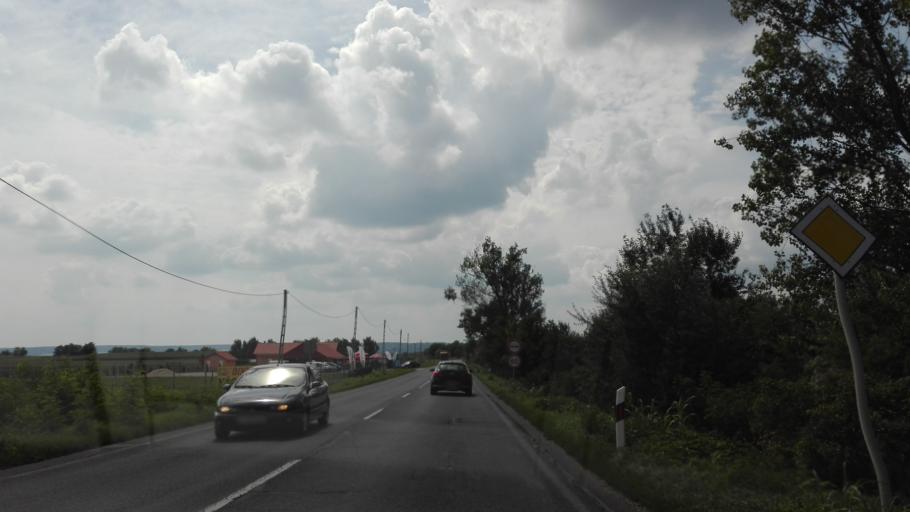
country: HU
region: Fejer
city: Cece
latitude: 46.7679
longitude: 18.6149
